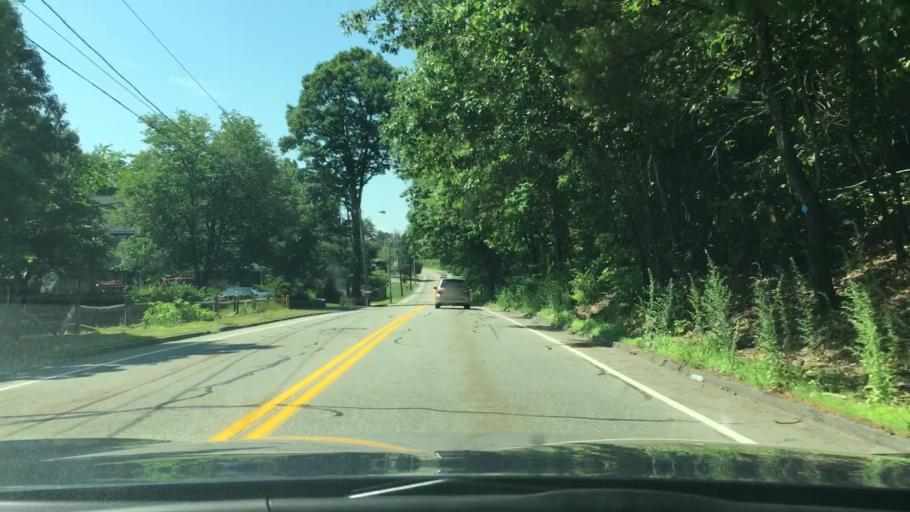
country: US
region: Massachusetts
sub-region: Middlesex County
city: Billerica
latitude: 42.5674
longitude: -71.2972
